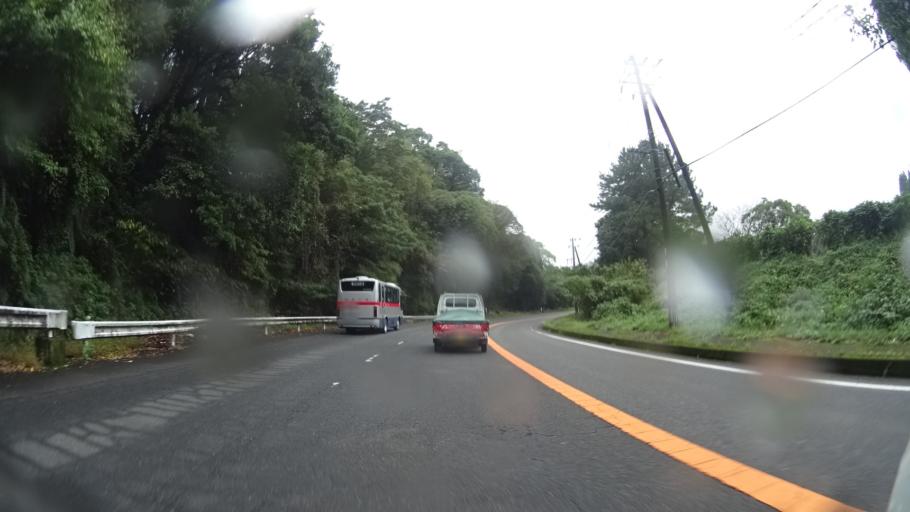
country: JP
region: Kagoshima
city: Kajiki
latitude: 31.7752
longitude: 130.6691
